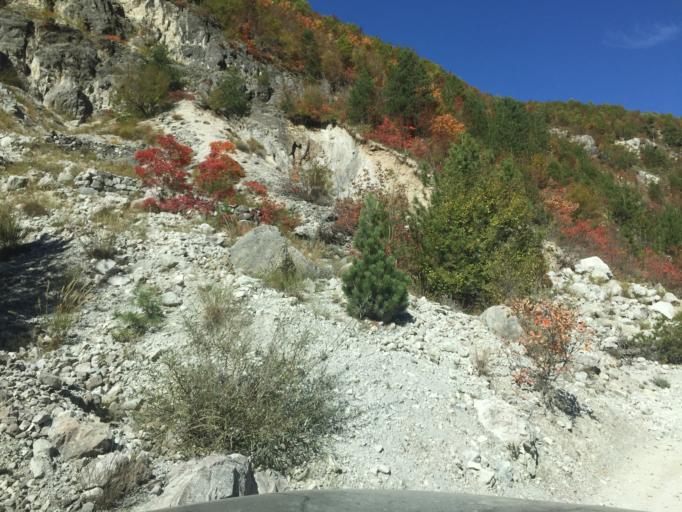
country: AL
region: Shkoder
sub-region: Rrethi i Shkodres
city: Nicaj-Shale
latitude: 42.3605
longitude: 19.7836
